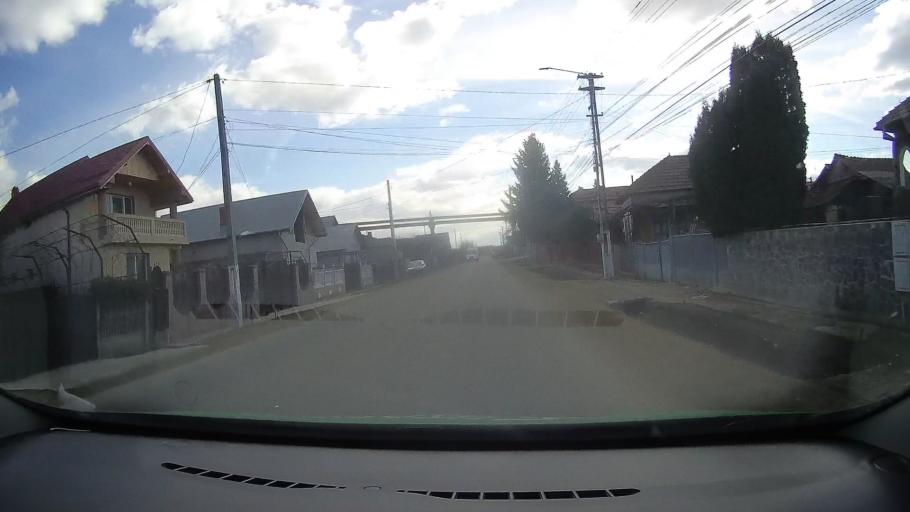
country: RO
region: Dambovita
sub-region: Comuna Doicesti
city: Doicesti
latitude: 44.9819
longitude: 25.3888
